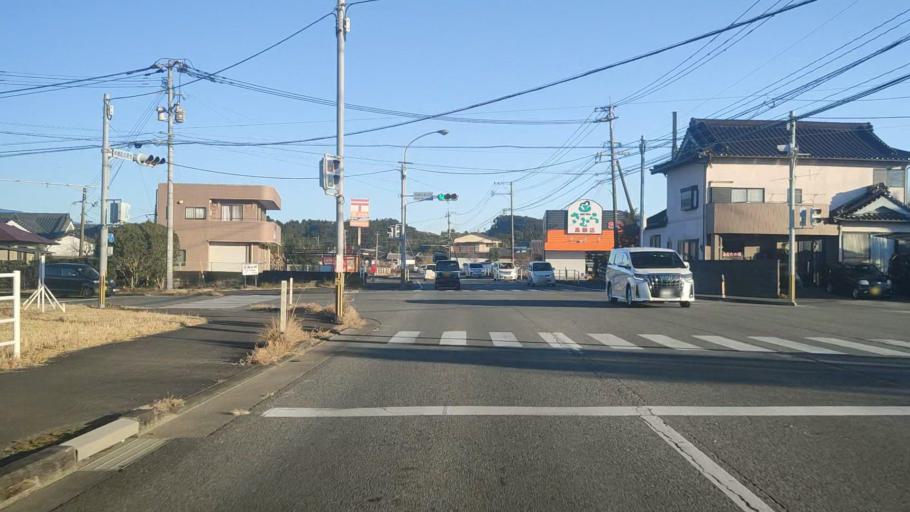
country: JP
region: Miyazaki
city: Takanabe
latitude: 32.1379
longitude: 131.5276
